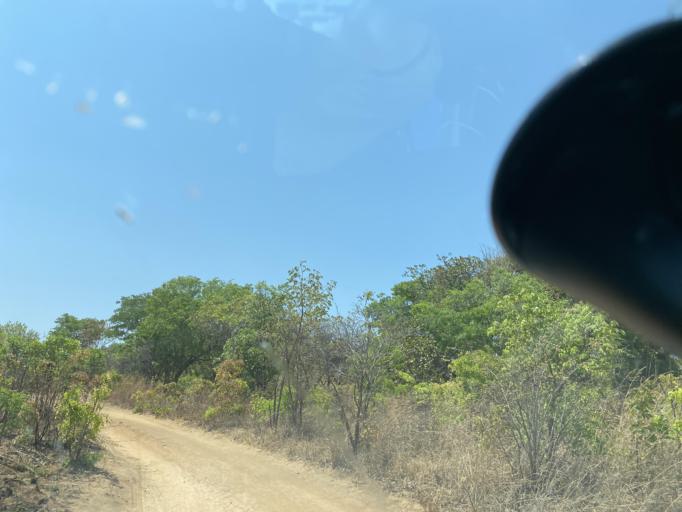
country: ZM
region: Lusaka
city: Chongwe
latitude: -15.4396
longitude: 29.2029
